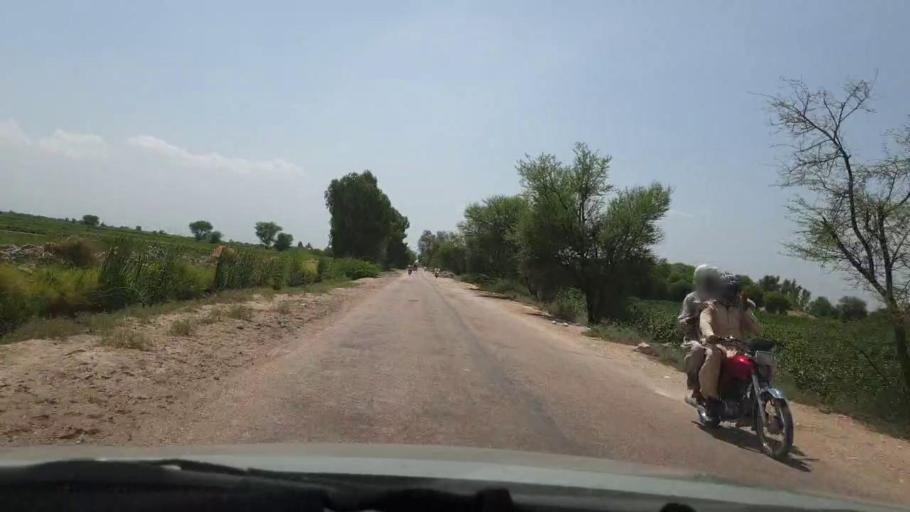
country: PK
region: Sindh
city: Pano Aqil
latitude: 27.6694
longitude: 69.1033
